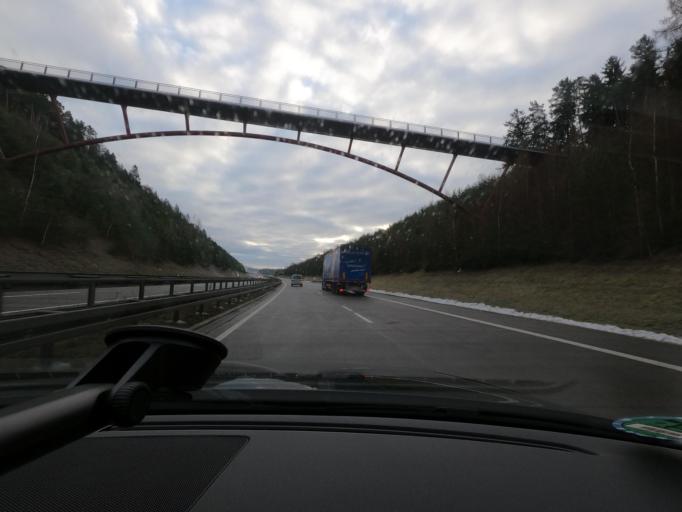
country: DE
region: Thuringia
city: Schleusingen
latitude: 50.4931
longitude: 10.8011
